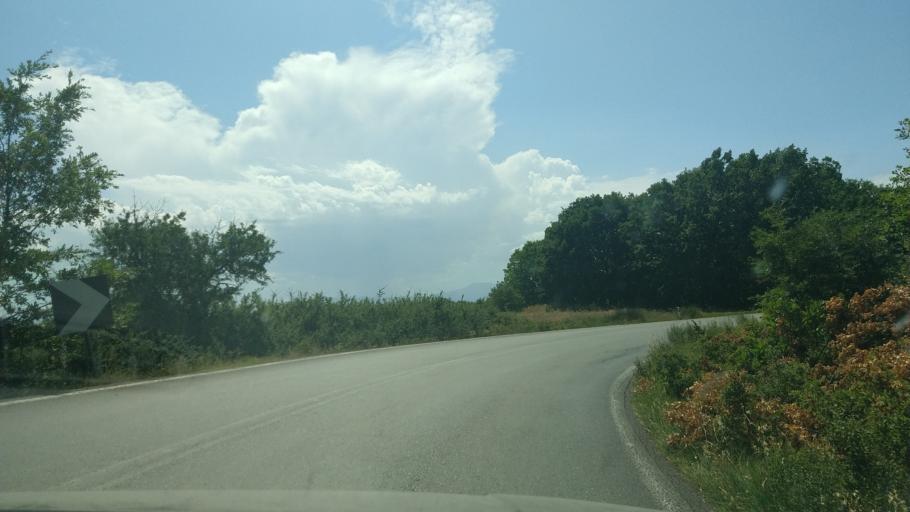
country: GR
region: West Macedonia
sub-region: Nomos Grevenon
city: Grevena
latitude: 40.0673
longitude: 21.4616
